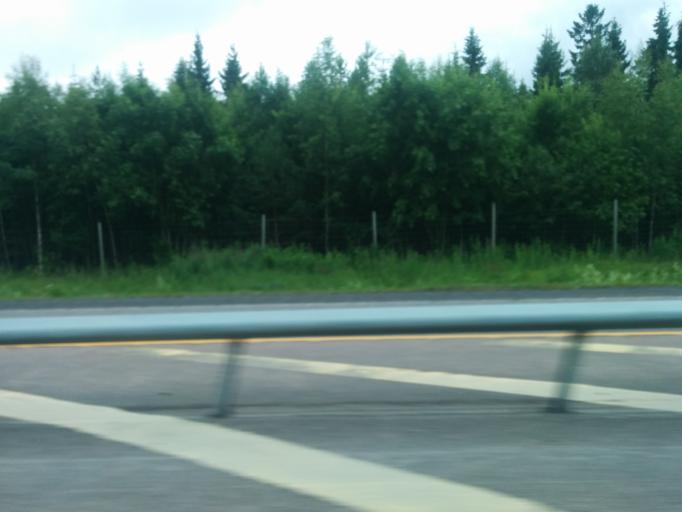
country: FI
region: Pirkanmaa
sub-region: Tampere
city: Orivesi
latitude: 61.7108
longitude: 24.5191
